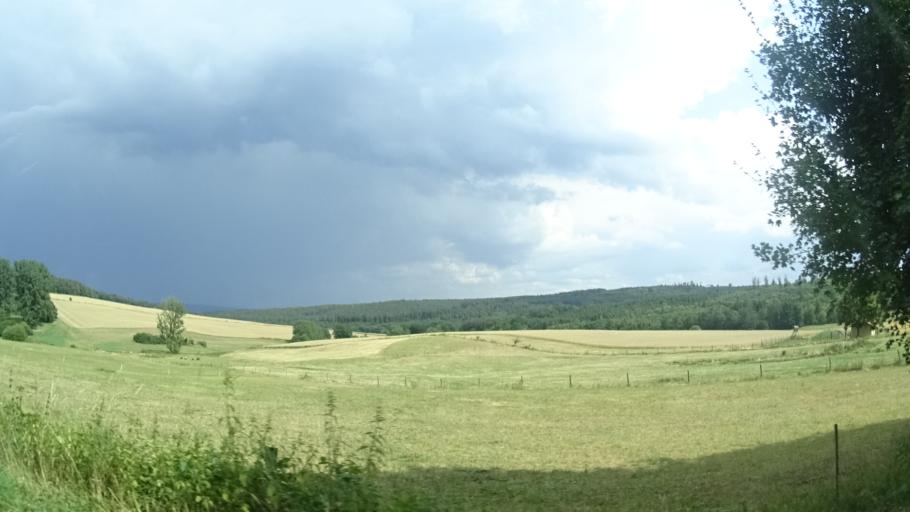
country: DE
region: Hesse
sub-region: Regierungsbezirk Giessen
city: Lauterbach
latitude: 50.5931
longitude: 9.4208
